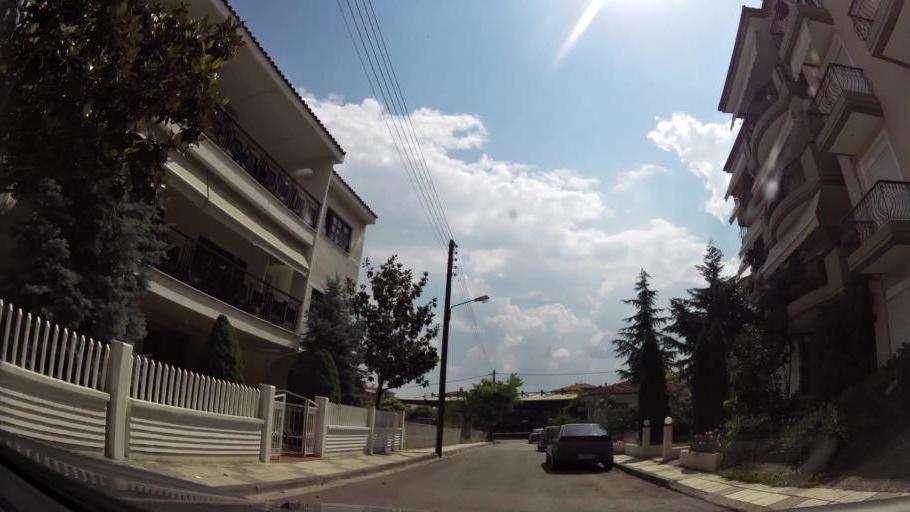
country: GR
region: West Macedonia
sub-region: Nomos Kozanis
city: Kozani
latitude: 40.3011
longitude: 21.7981
